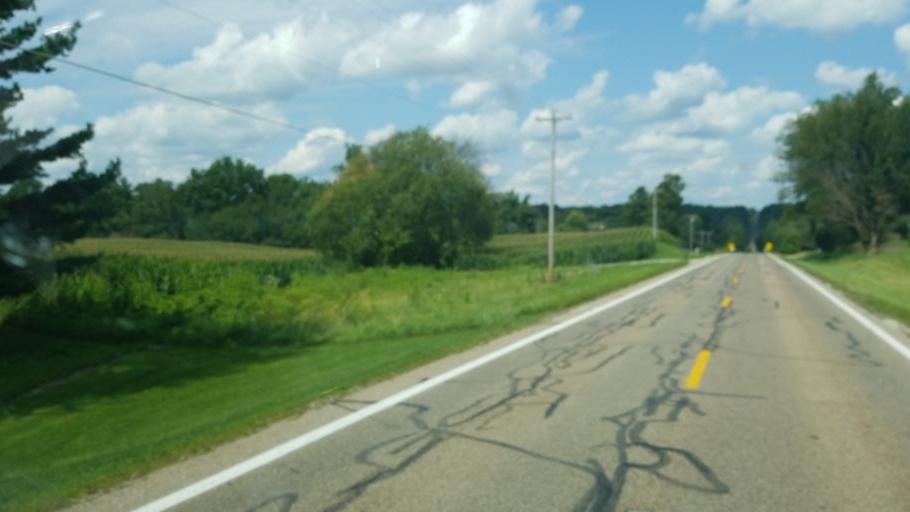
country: US
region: Ohio
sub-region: Richland County
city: Lexington
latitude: 40.6995
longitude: -82.6653
